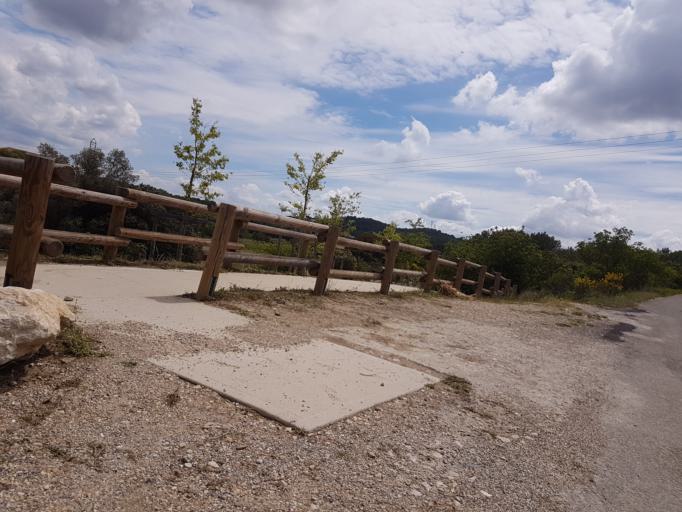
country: FR
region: Languedoc-Roussillon
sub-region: Departement du Gard
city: Vallabregues
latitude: 43.8362
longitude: 4.6180
